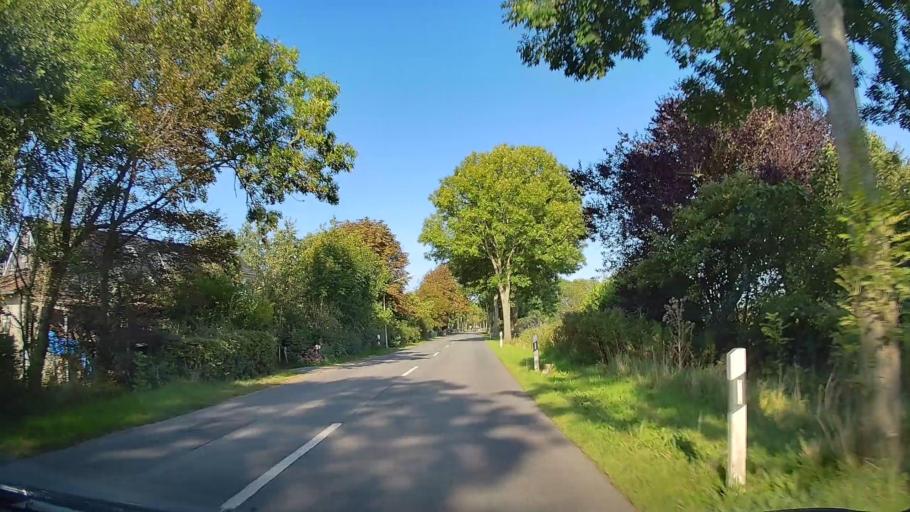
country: DE
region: Lower Saxony
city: Cappel
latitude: 53.7475
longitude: 8.5583
